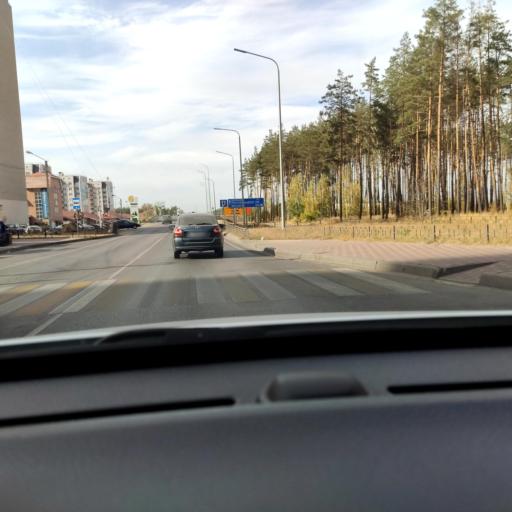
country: RU
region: Voronezj
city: Somovo
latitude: 51.7422
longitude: 39.3157
